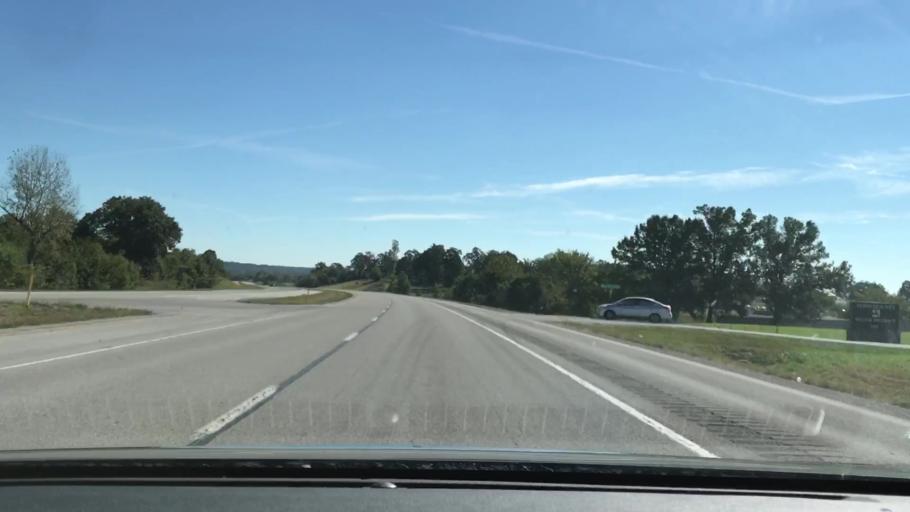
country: US
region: Kentucky
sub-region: Todd County
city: Elkton
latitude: 36.8213
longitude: -87.1920
